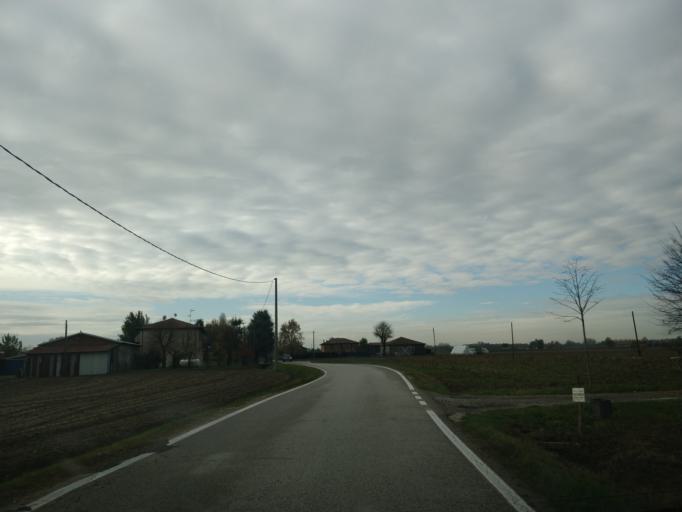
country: IT
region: Emilia-Romagna
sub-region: Provincia di Bologna
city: Argelato
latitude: 44.6318
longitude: 11.3205
